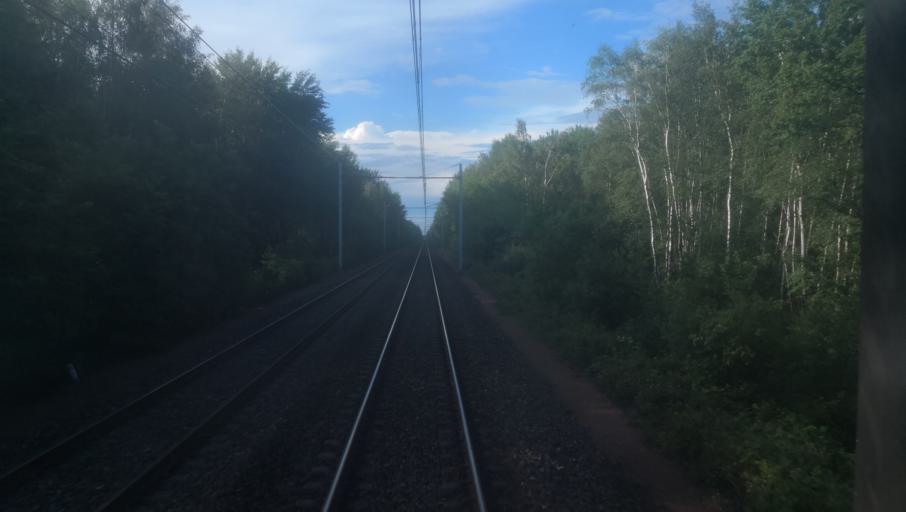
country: FR
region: Centre
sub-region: Departement du Loir-et-Cher
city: Salbris
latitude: 47.3704
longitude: 2.0490
